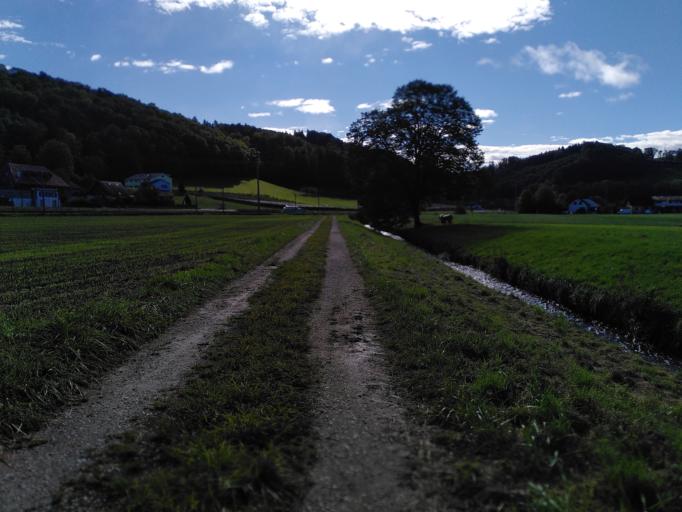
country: CH
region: Bern
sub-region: Oberaargau
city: Seeberg
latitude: 47.1481
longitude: 7.6941
